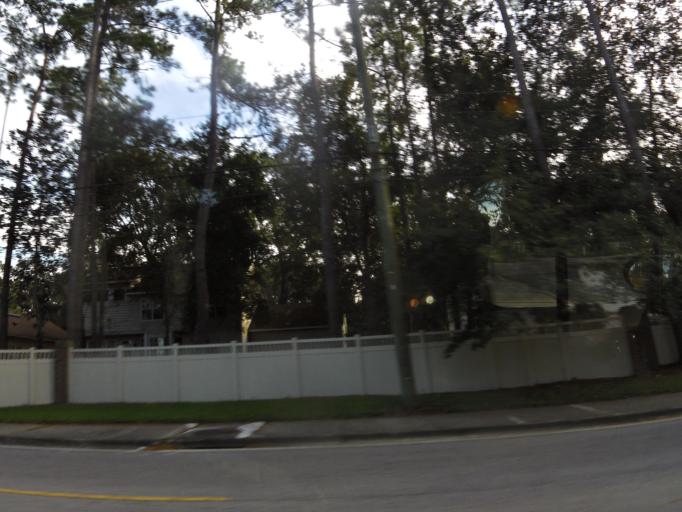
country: US
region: Florida
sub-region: Saint Johns County
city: Fruit Cove
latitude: 30.1597
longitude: -81.6040
